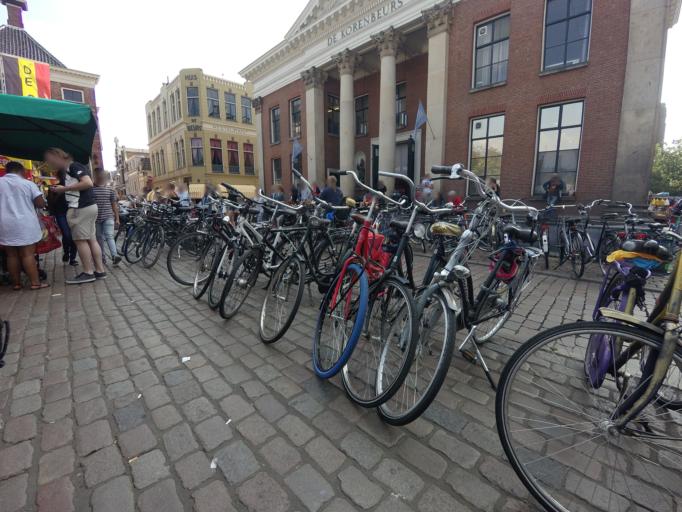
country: NL
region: Groningen
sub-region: Gemeente Groningen
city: Groningen
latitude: 53.2170
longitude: 6.5639
